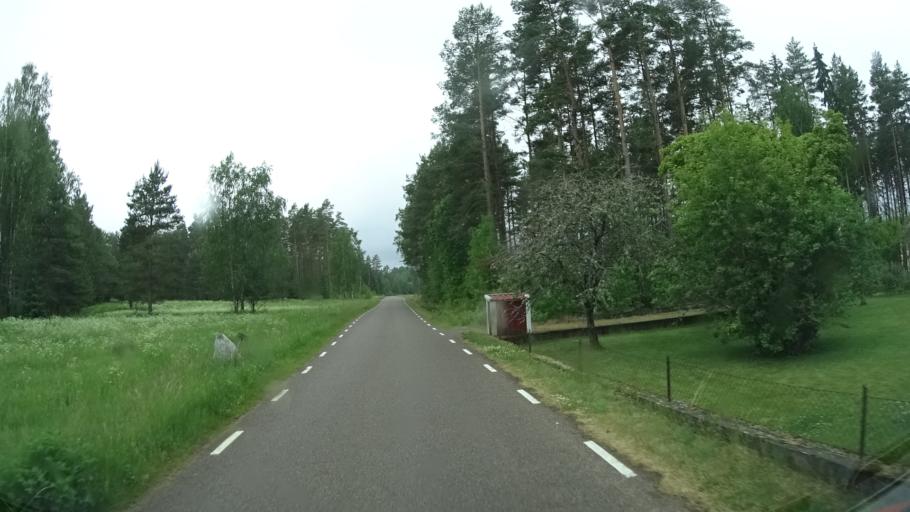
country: SE
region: Kalmar
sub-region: Vimmerby Kommun
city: Sodra Vi
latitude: 57.7023
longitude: 15.7387
